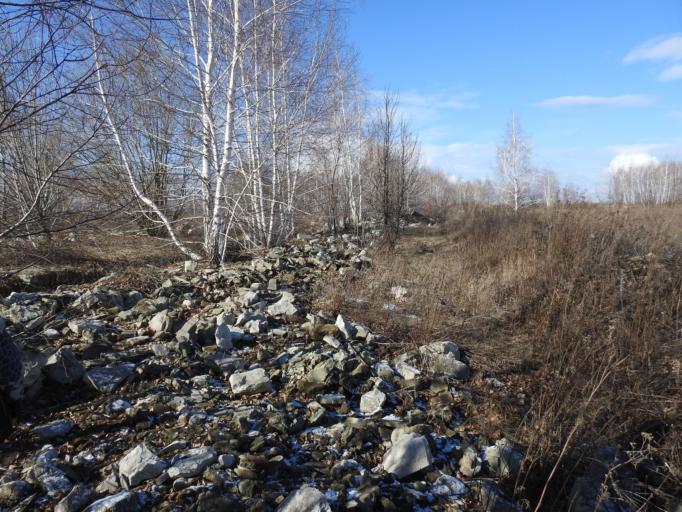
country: RU
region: Saratov
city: Krasnyy Oktyabr'
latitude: 51.3892
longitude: 45.7259
